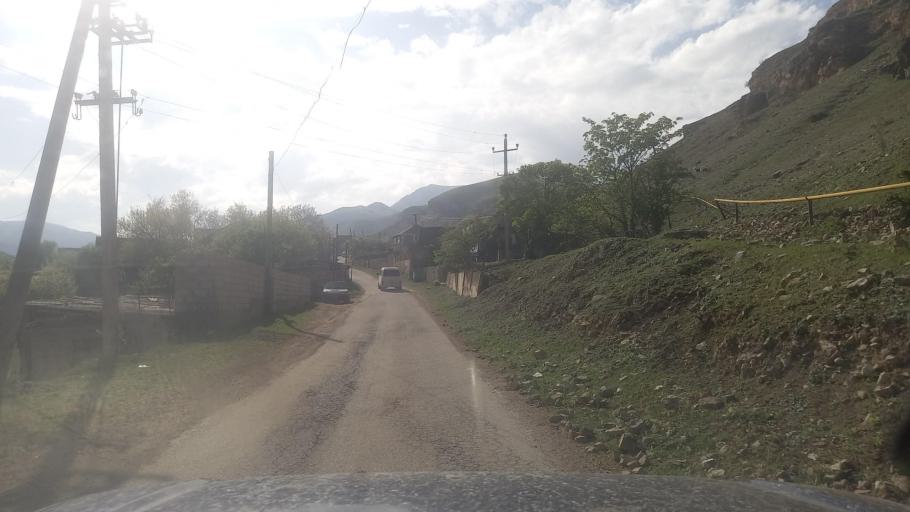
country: RU
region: Kabardino-Balkariya
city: Kamennomostskoye
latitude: 43.7255
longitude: 42.9196
